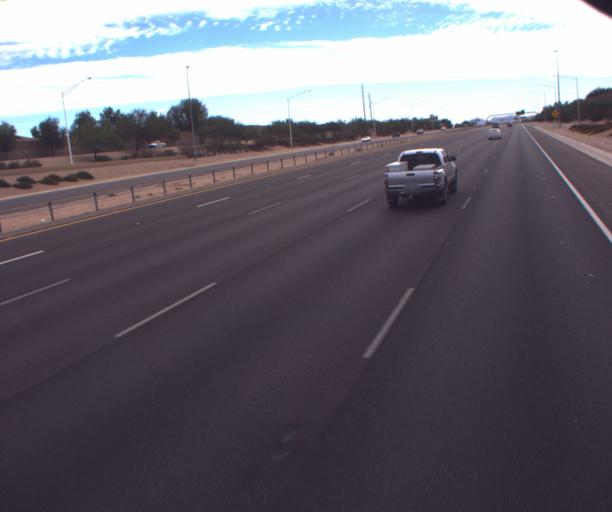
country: US
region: Arizona
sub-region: Pinal County
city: Apache Junction
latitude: 33.3631
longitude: -111.6443
